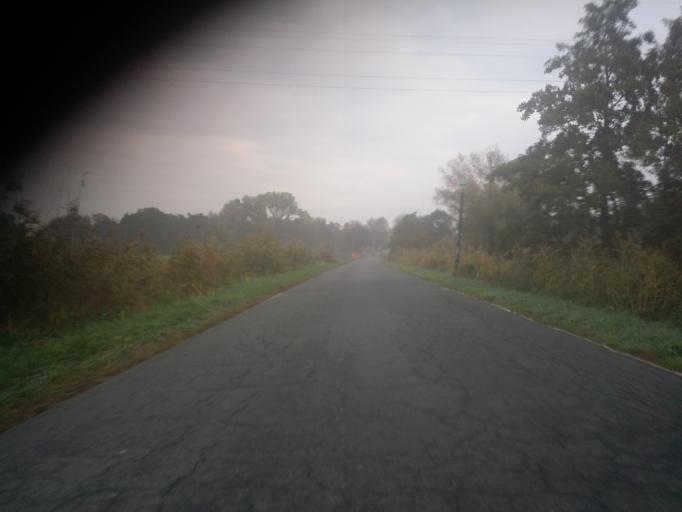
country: DE
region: Lower Saxony
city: Lilienthal
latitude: 53.1274
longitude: 8.8616
